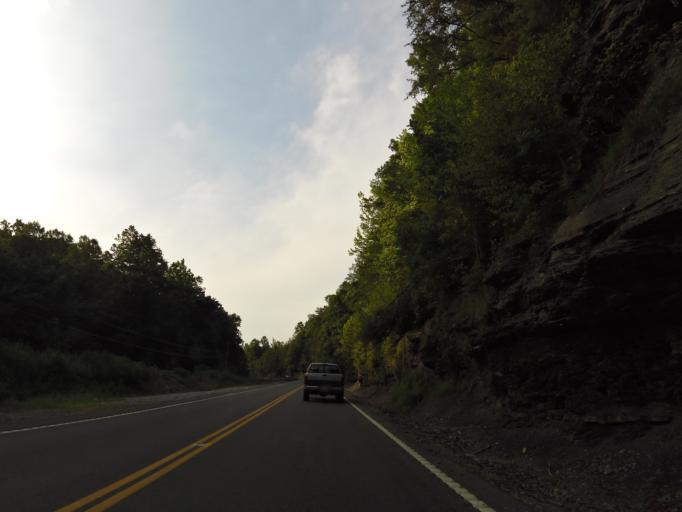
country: US
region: Tennessee
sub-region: Morgan County
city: Coalfield
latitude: 36.0526
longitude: -84.4392
